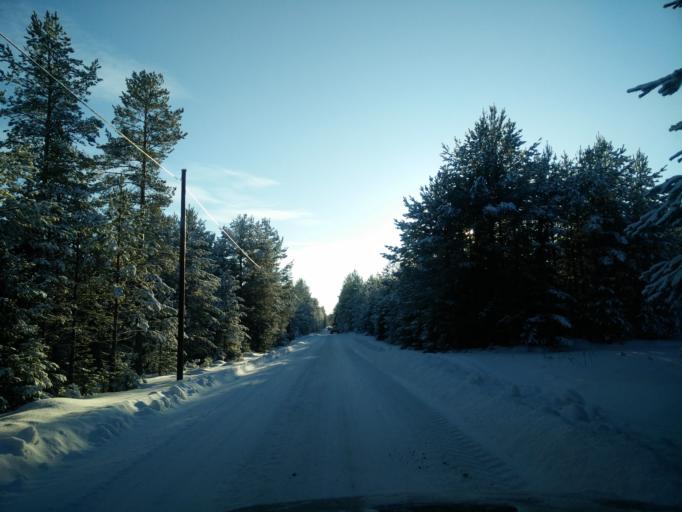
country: SE
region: Vaesternorrland
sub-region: Sundsvalls Kommun
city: Njurundabommen
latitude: 62.2160
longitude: 17.4935
